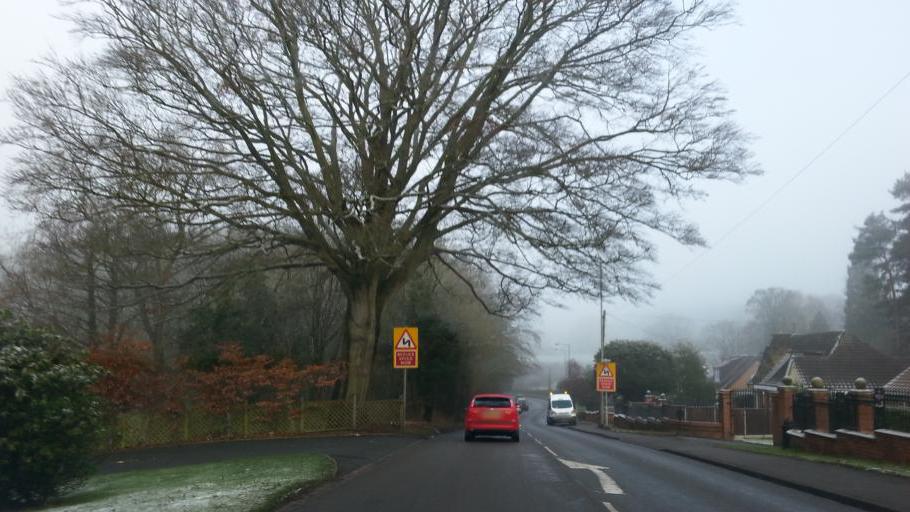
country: GB
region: England
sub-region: Staffordshire
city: Biddulph
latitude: 53.1310
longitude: -2.1660
